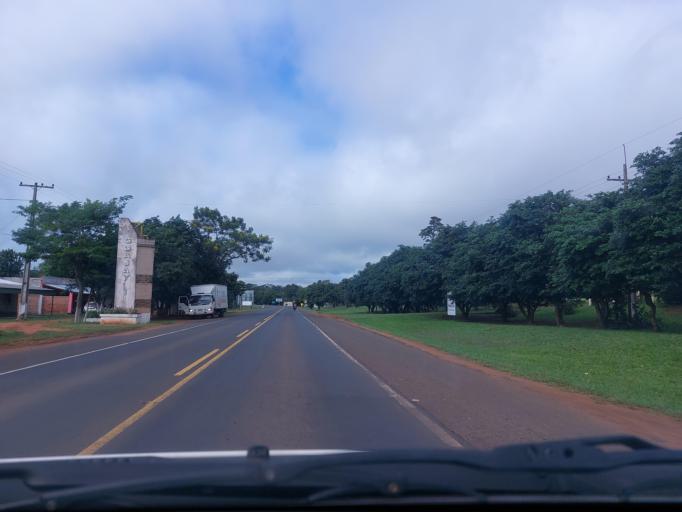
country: PY
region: San Pedro
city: Guayaybi
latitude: -24.5812
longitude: -56.4022
